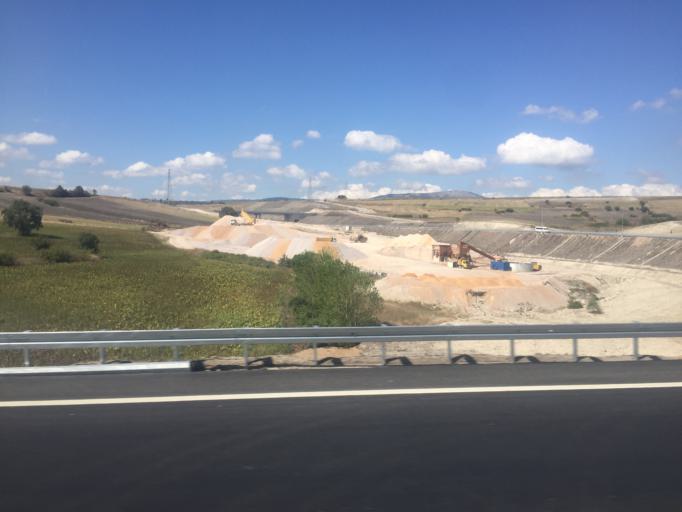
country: TR
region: Balikesir
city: Susurluk
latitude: 39.9672
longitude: 28.1634
